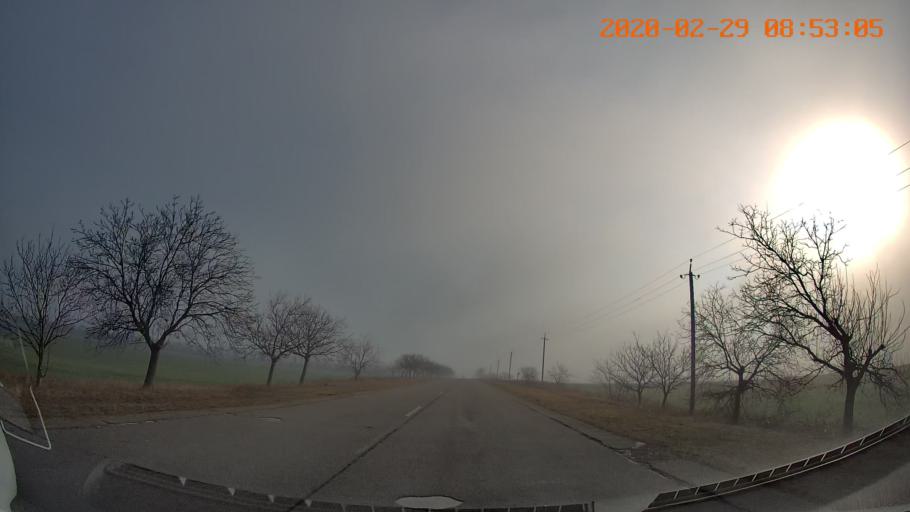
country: MD
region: Telenesti
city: Tiraspolul Nou
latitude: 46.9250
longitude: 29.5503
